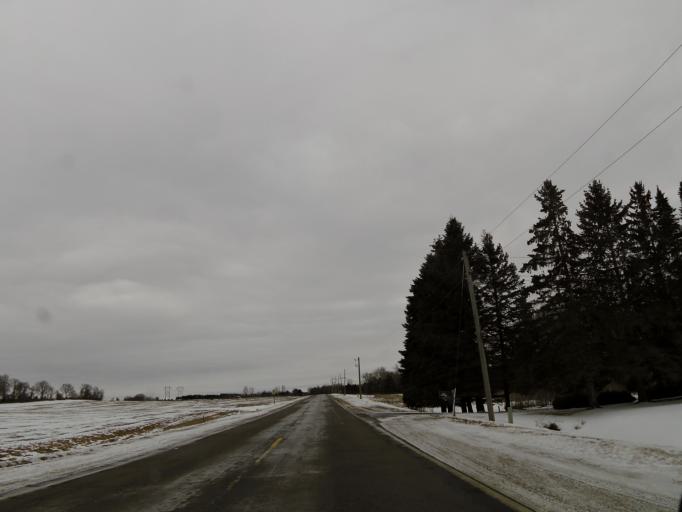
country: US
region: Minnesota
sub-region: Washington County
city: Cottage Grove
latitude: 44.8275
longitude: -92.8900
